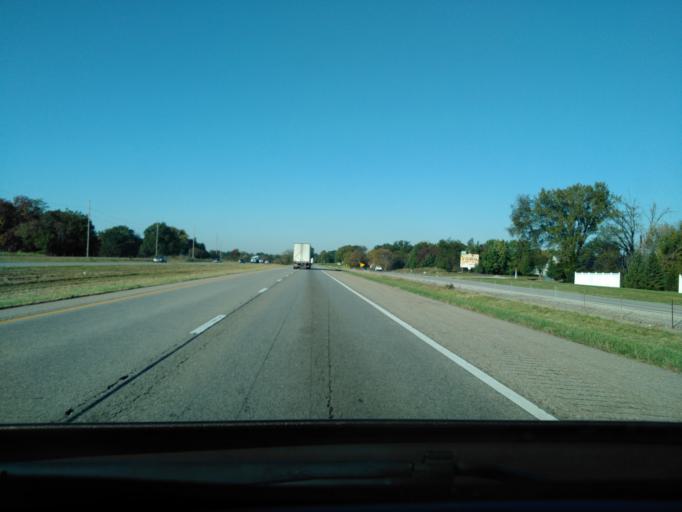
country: US
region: Illinois
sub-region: Bond County
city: Greenville
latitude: 38.8467
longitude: -89.4779
